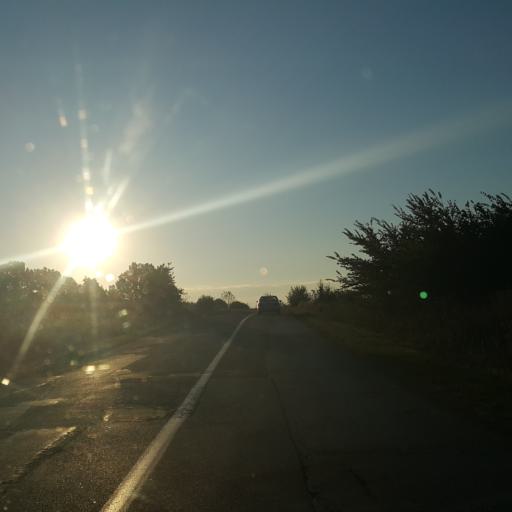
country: RS
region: Central Serbia
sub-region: Borski Okrug
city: Negotin
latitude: 44.2086
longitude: 22.4167
